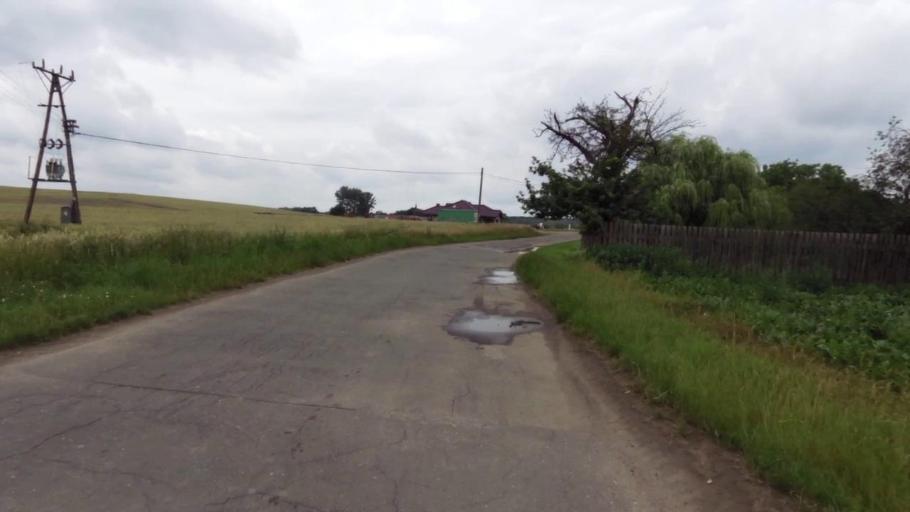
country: PL
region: West Pomeranian Voivodeship
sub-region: Powiat pyrzycki
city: Lipiany
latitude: 52.9672
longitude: 14.9424
